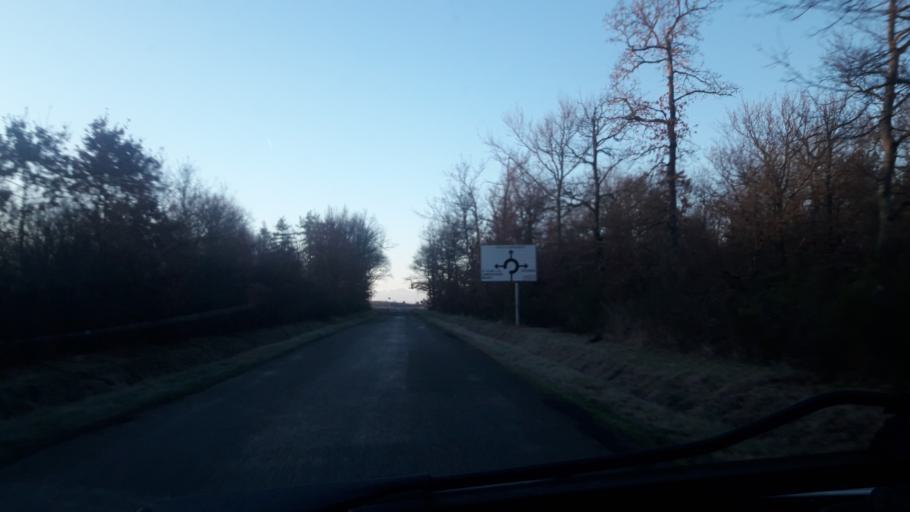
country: FR
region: Midi-Pyrenees
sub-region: Departement de la Haute-Garonne
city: Lherm
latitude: 43.4417
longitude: 1.1721
